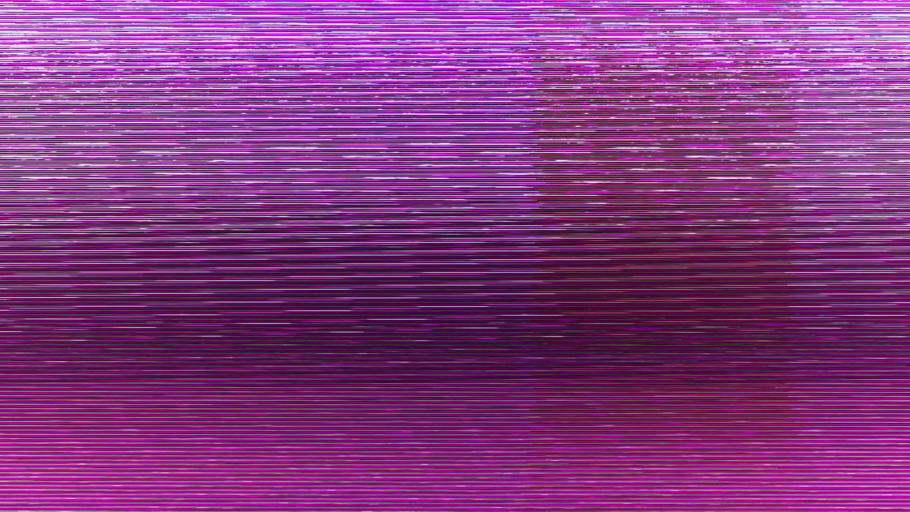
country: US
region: Michigan
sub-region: Washtenaw County
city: Ypsilanti
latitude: 42.2302
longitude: -83.5631
